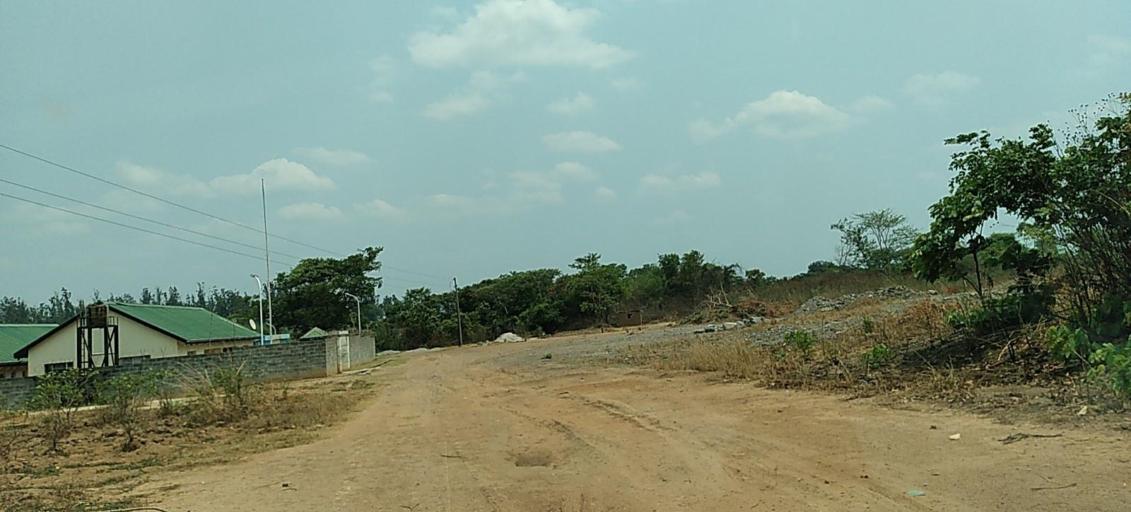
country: ZM
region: Copperbelt
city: Kalulushi
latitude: -12.7605
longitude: 28.0310
